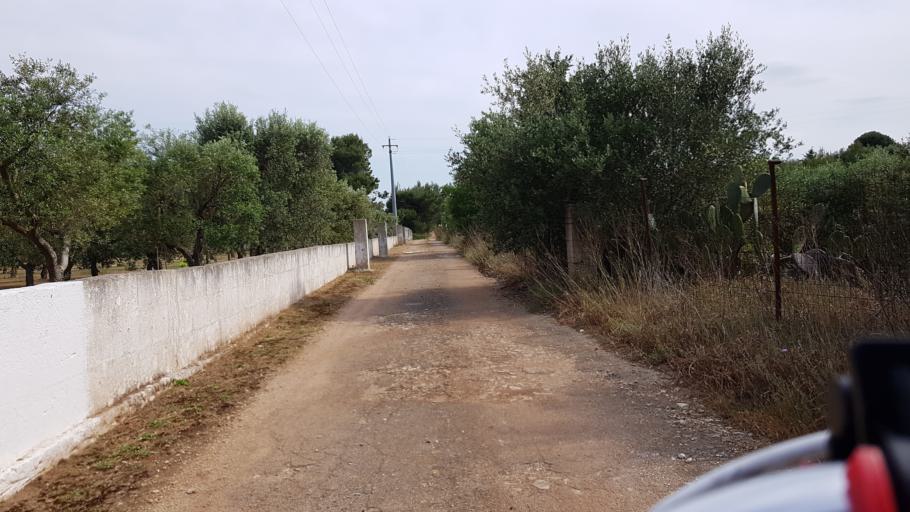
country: IT
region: Apulia
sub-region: Provincia di Brindisi
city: San Vito dei Normanni
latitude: 40.6522
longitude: 17.7712
